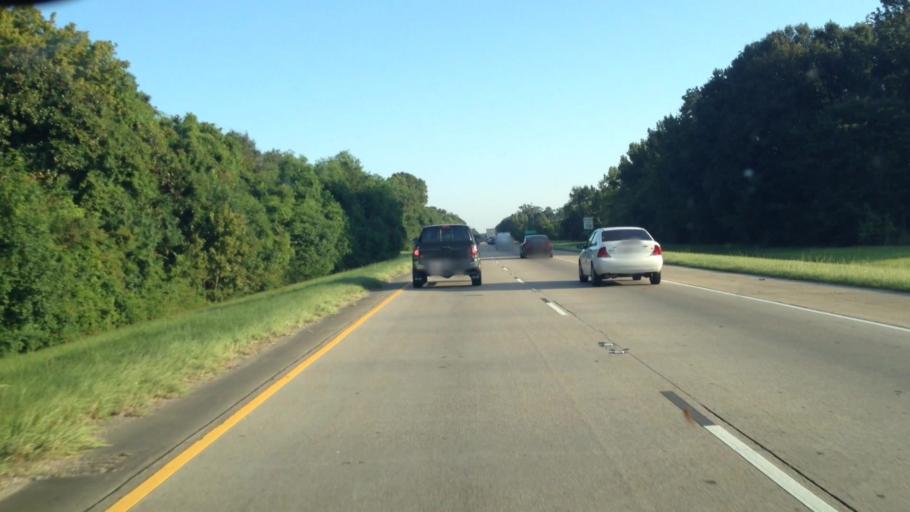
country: US
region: Louisiana
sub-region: Ascension Parish
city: Prairieville
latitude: 30.2805
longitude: -90.9886
